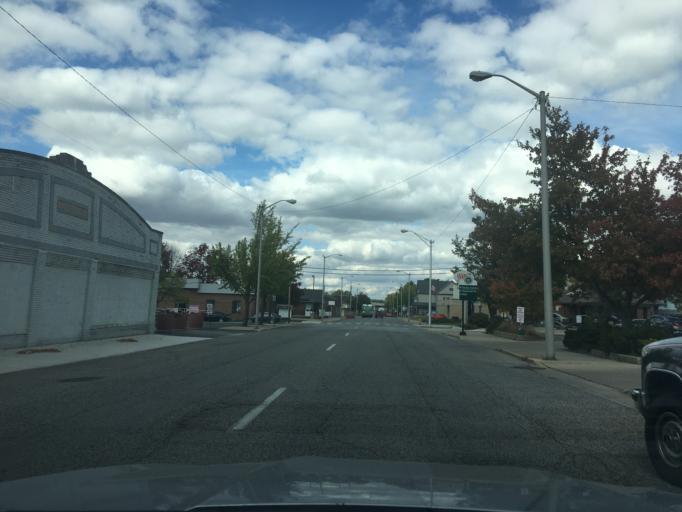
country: US
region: Indiana
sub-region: Tippecanoe County
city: West Lafayette
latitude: 40.4203
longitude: -86.8931
